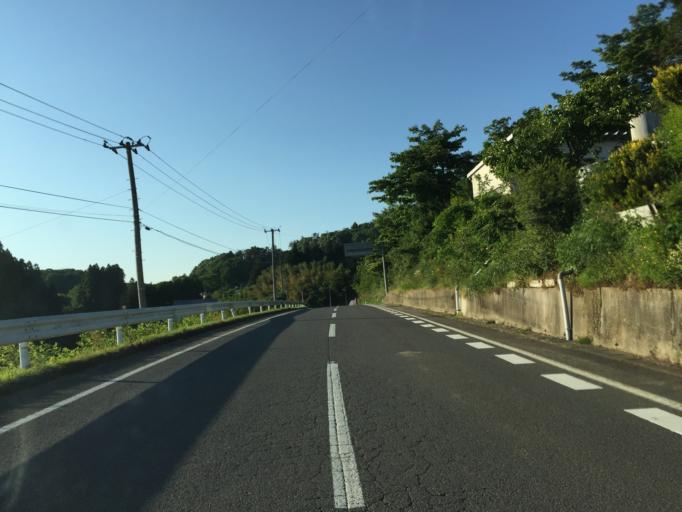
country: JP
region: Fukushima
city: Ishikawa
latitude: 37.0168
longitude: 140.4354
